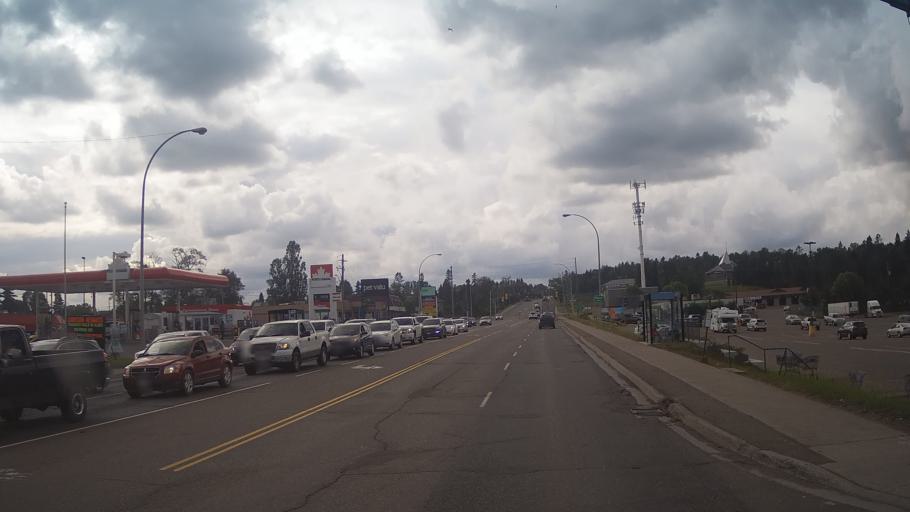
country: CA
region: Ontario
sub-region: Thunder Bay District
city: Thunder Bay
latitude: 48.4516
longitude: -89.2538
